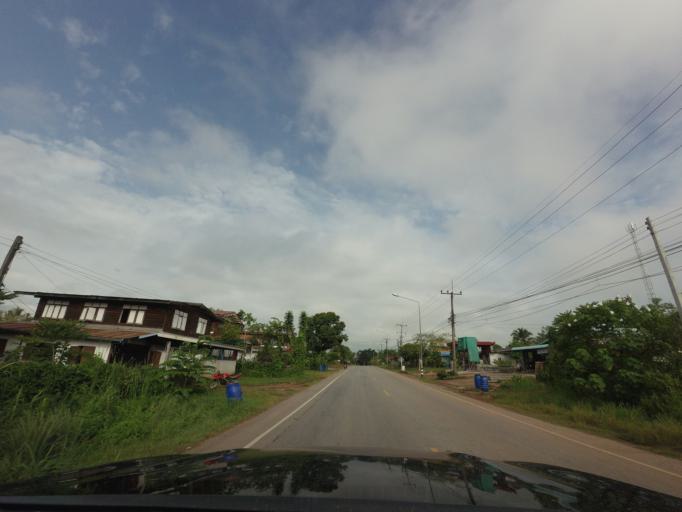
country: TH
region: Changwat Udon Thani
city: Nam Som
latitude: 17.8297
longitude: 102.2644
